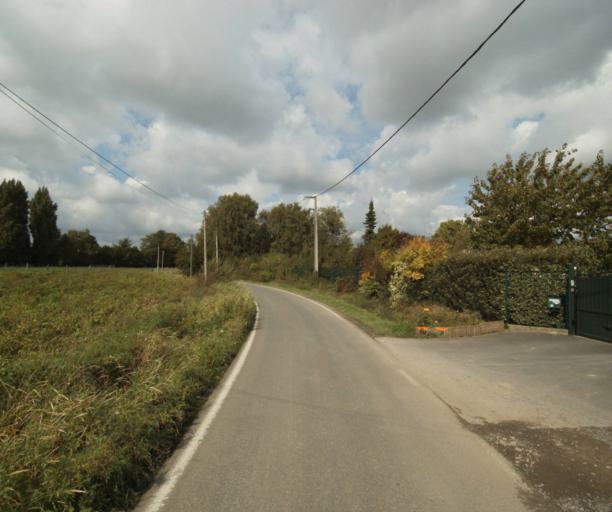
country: FR
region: Nord-Pas-de-Calais
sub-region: Departement du Nord
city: Perenchies
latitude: 50.6730
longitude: 2.9539
